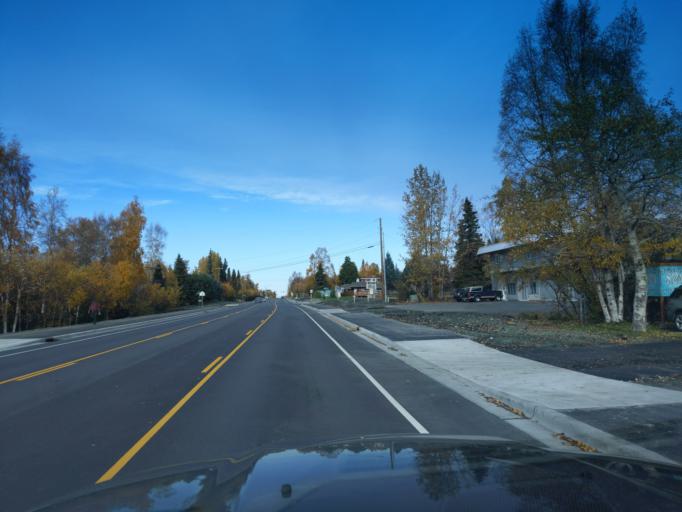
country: US
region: Alaska
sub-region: Anchorage Municipality
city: Anchorage
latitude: 61.1472
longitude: -149.9518
